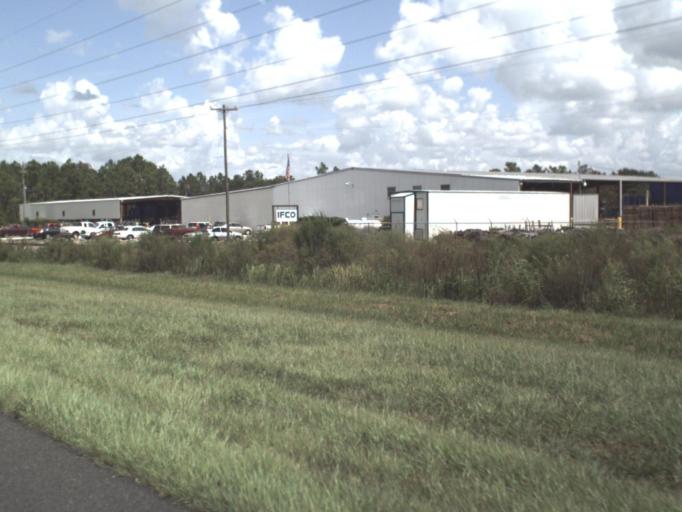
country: US
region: Florida
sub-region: Polk County
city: Bartow
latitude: 27.8265
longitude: -81.8223
